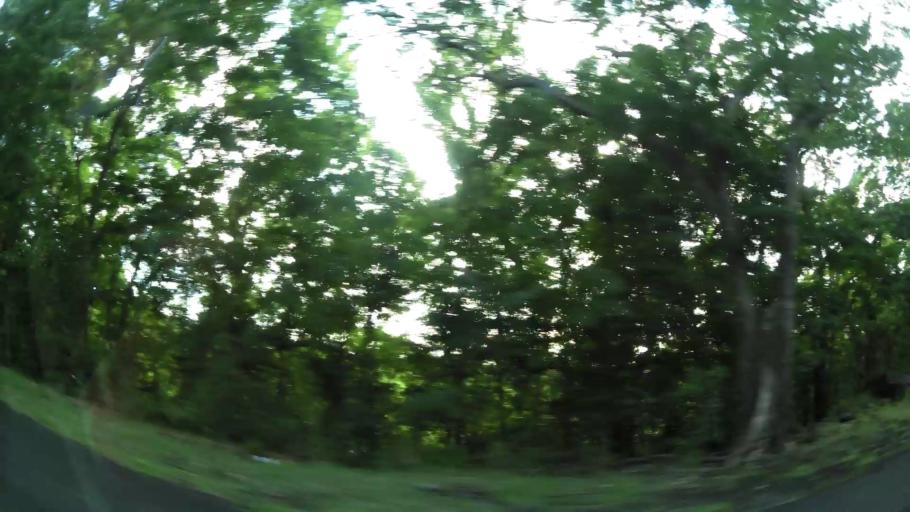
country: GP
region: Guadeloupe
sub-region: Guadeloupe
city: Pointe-Noire
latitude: 16.1838
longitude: -61.7696
